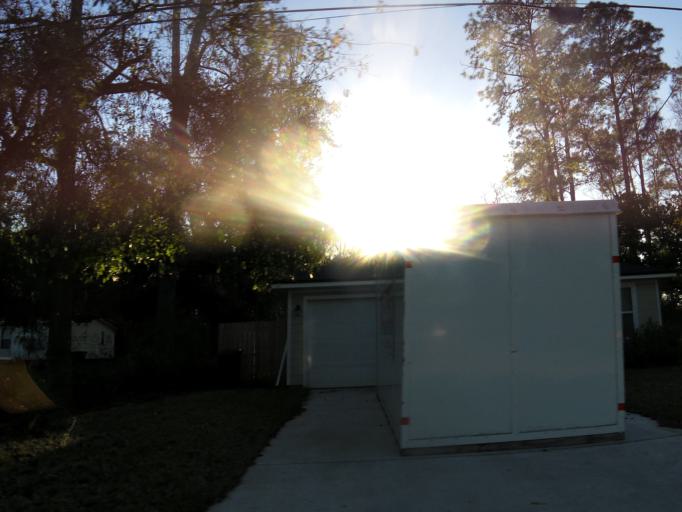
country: US
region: Florida
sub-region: Saint Johns County
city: Fruit Cove
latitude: 30.2024
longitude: -81.5765
